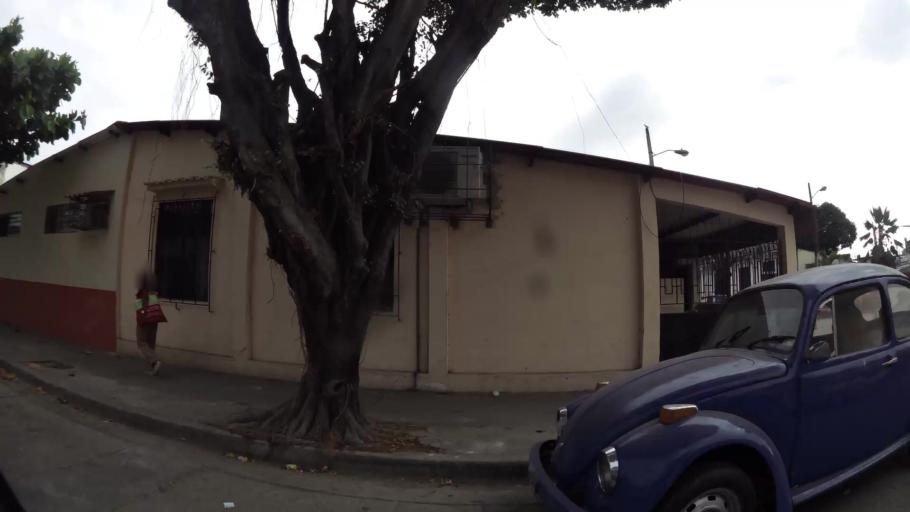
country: EC
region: Guayas
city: Eloy Alfaro
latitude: -2.1367
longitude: -79.8874
